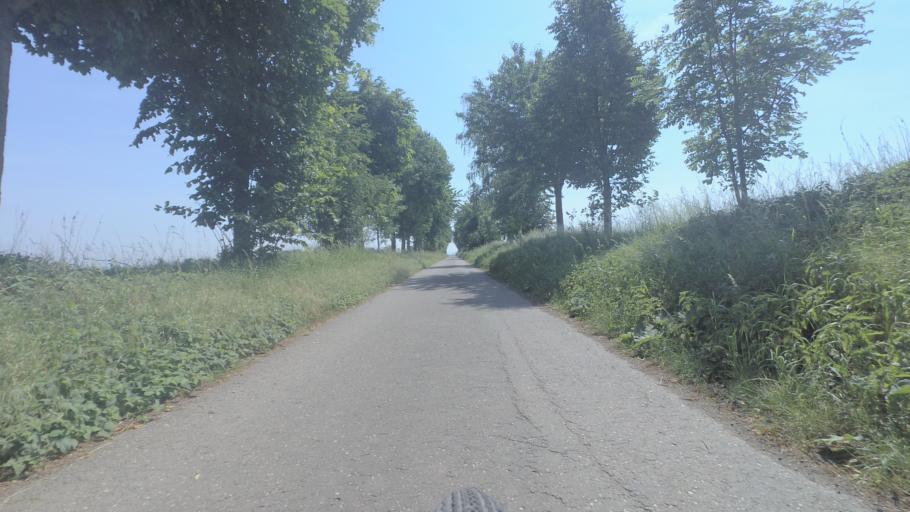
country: DE
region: Saxony-Anhalt
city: Gross Bornecke
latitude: 51.8527
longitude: 11.4875
